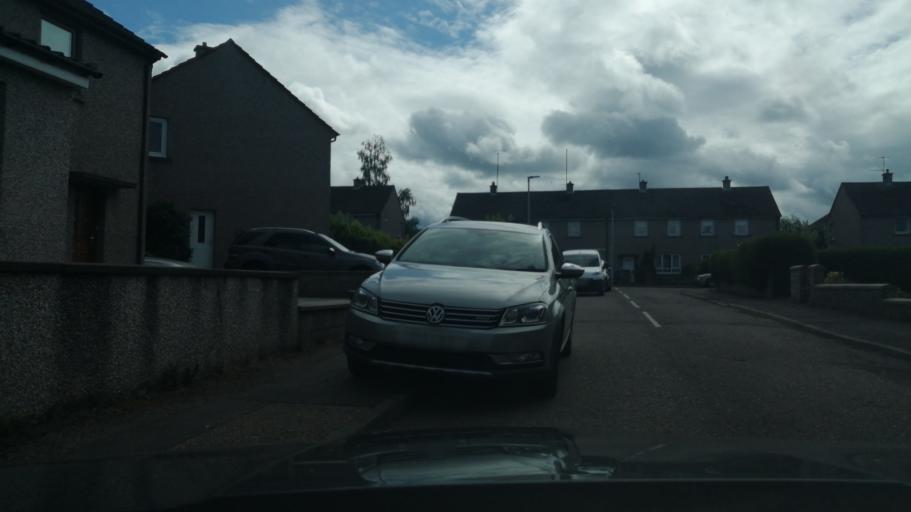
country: GB
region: Scotland
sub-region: Moray
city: Elgin
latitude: 57.6567
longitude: -3.3092
